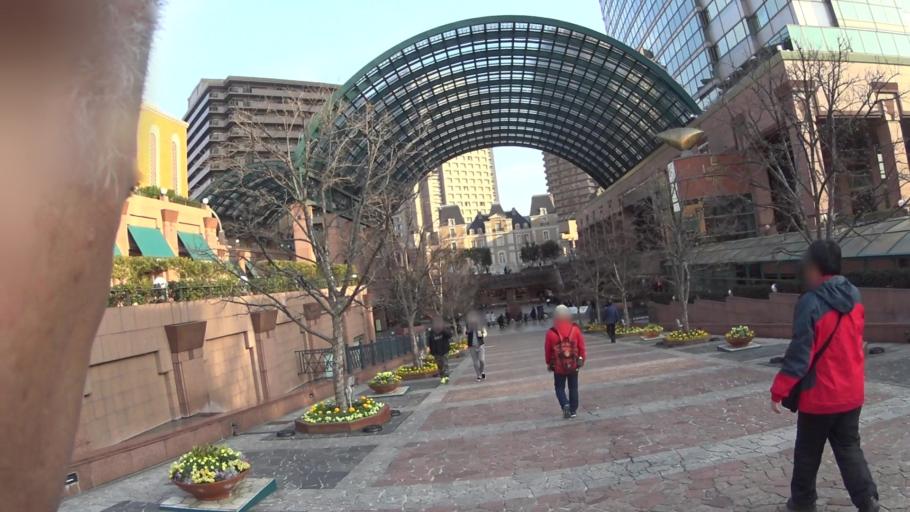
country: JP
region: Tokyo
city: Tokyo
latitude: 35.6429
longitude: 139.7137
